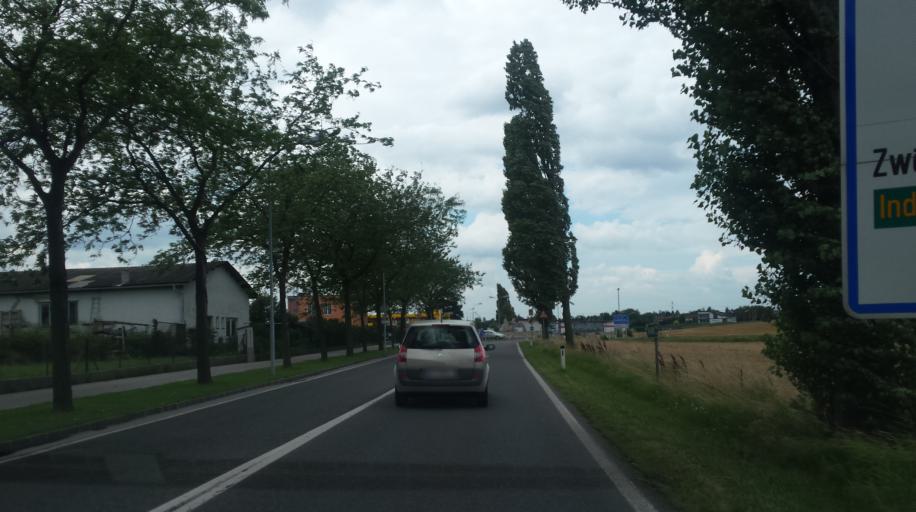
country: AT
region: Lower Austria
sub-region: Politischer Bezirk Wien-Umgebung
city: Zwolfaxing
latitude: 48.1186
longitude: 16.4547
